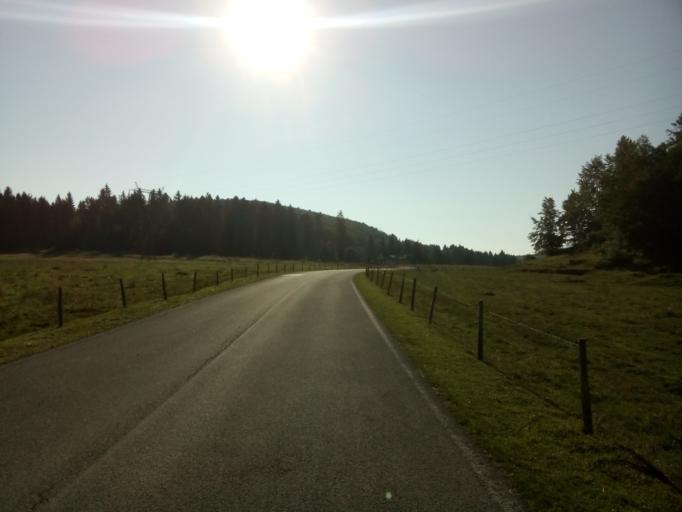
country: IT
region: Veneto
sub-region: Provincia di Vicenza
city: Conco
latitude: 45.8218
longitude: 11.6164
